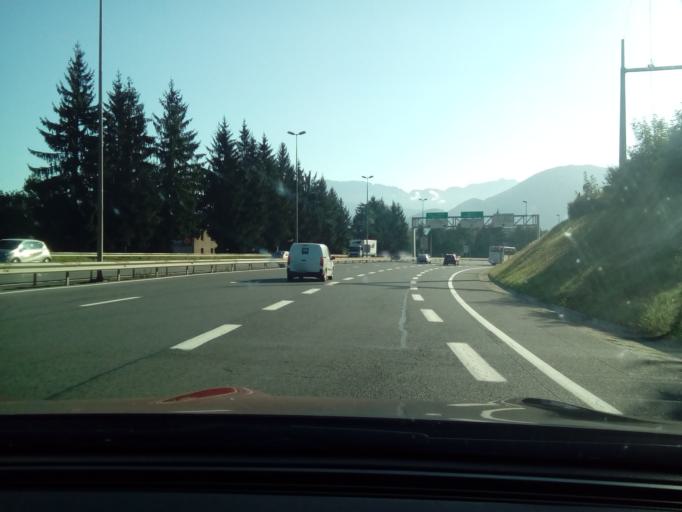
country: FR
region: Rhone-Alpes
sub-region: Departement de la Haute-Savoie
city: Cran-Gevrier
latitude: 45.9002
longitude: 6.0980
